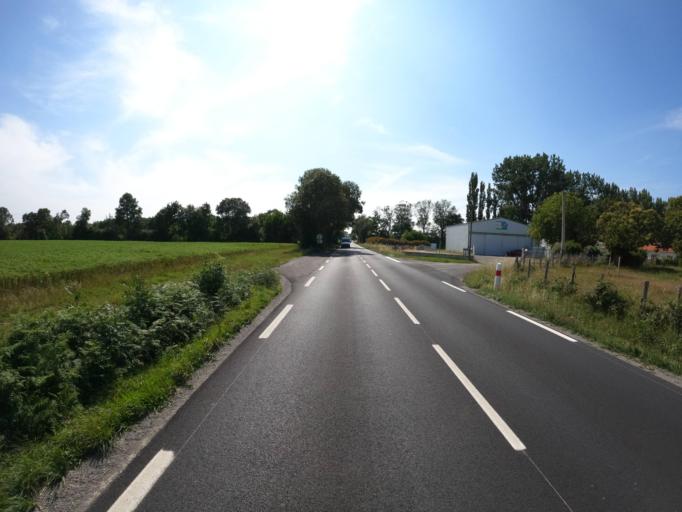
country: FR
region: Pays de la Loire
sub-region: Departement de la Loire-Atlantique
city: Paulx
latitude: 46.9930
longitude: -1.7644
